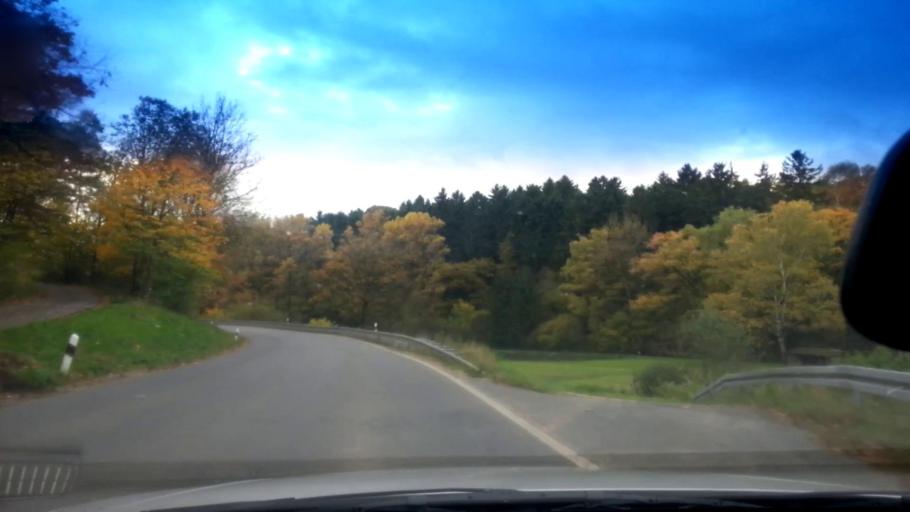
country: DE
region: Bavaria
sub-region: Upper Franconia
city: Wonsees
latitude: 49.9985
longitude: 11.2994
